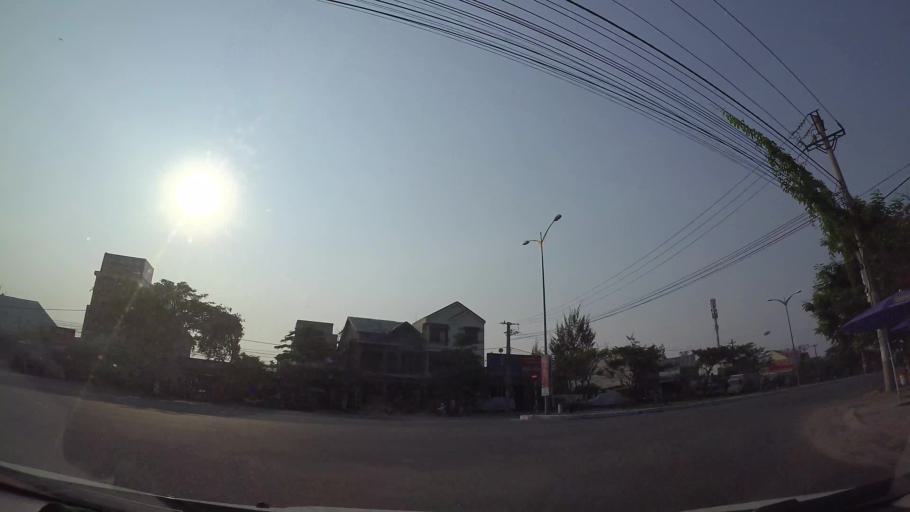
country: VN
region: Da Nang
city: Ngu Hanh Son
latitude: 15.9717
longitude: 108.2550
